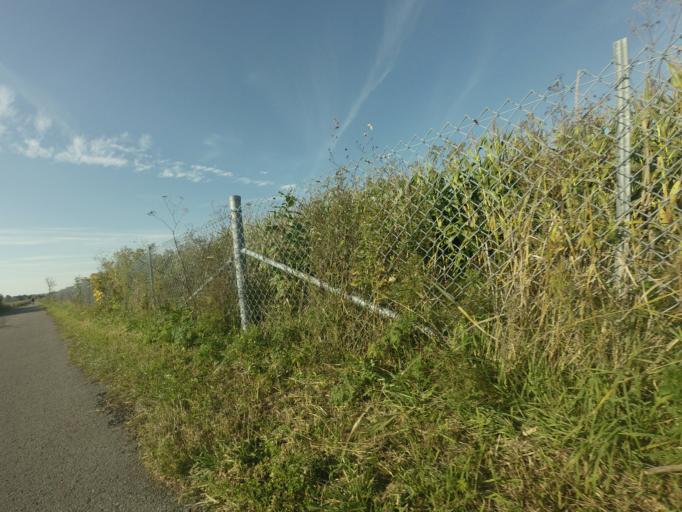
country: CA
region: Quebec
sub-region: Laurentides
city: Saint-Jerome
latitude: 45.7461
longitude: -73.9659
